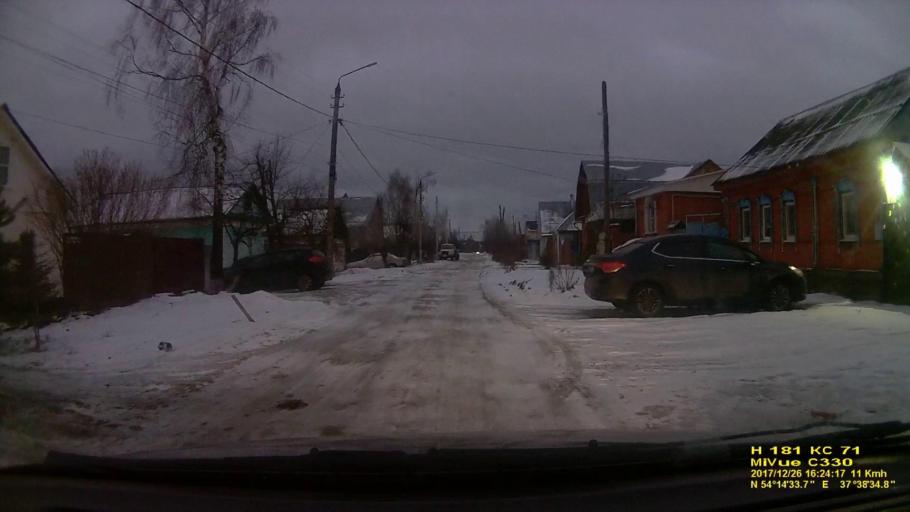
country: RU
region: Tula
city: Gorelki
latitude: 54.2427
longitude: 37.6430
